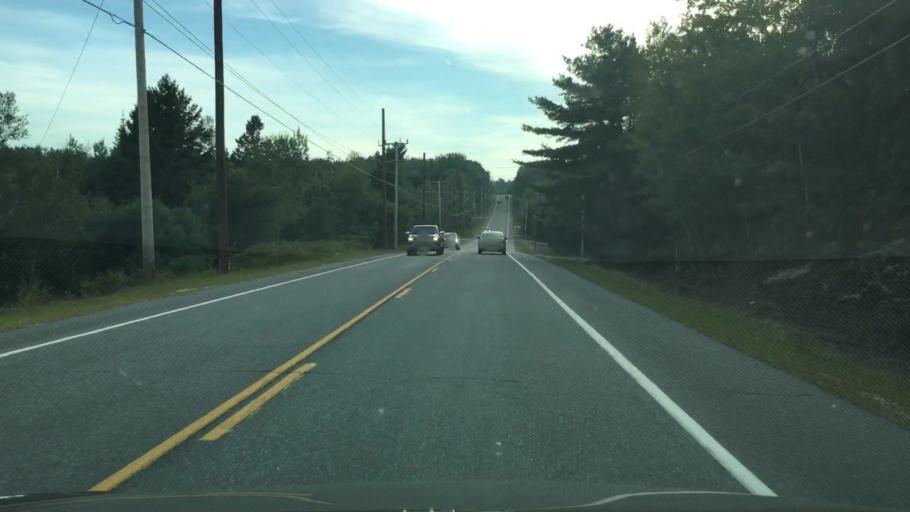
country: US
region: Maine
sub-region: Hancock County
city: Surry
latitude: 44.4586
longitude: -68.5436
